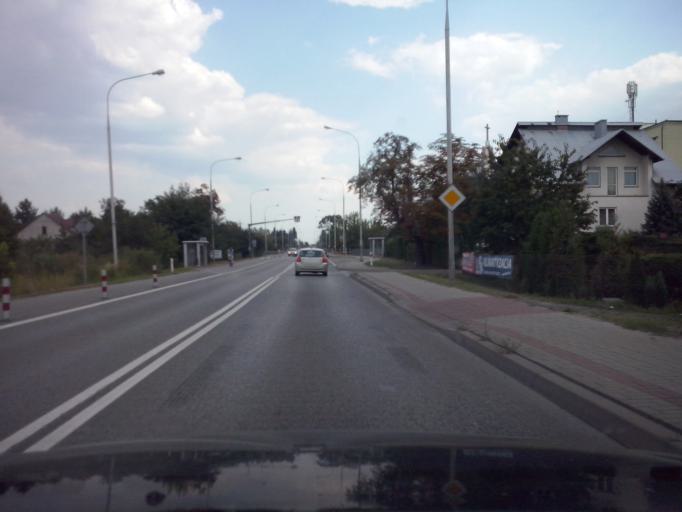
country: PL
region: Subcarpathian Voivodeship
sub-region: Powiat stalowowolski
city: Stalowa Wola
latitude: 50.5444
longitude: 22.0825
